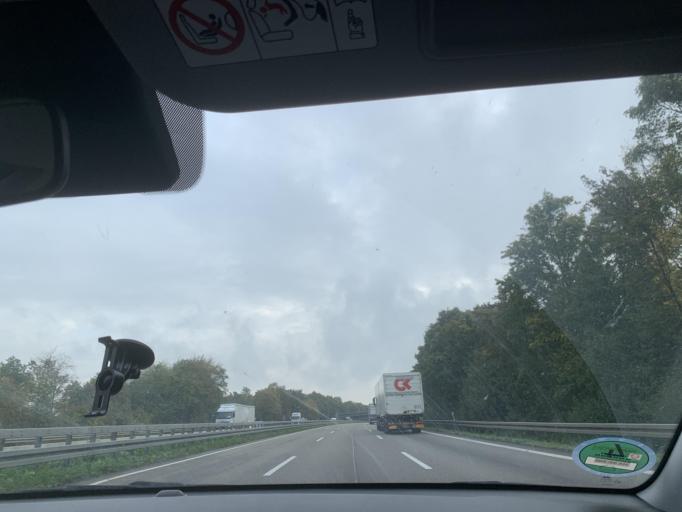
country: DE
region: Baden-Wuerttemberg
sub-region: Regierungsbezirk Stuttgart
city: Ohringen
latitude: 49.2037
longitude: 9.4689
